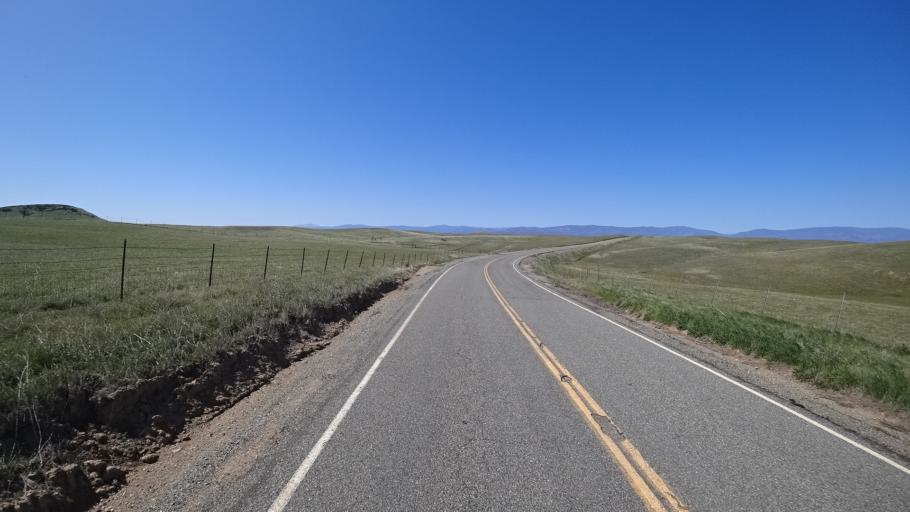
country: US
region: California
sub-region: Glenn County
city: Orland
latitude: 39.8288
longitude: -122.3524
